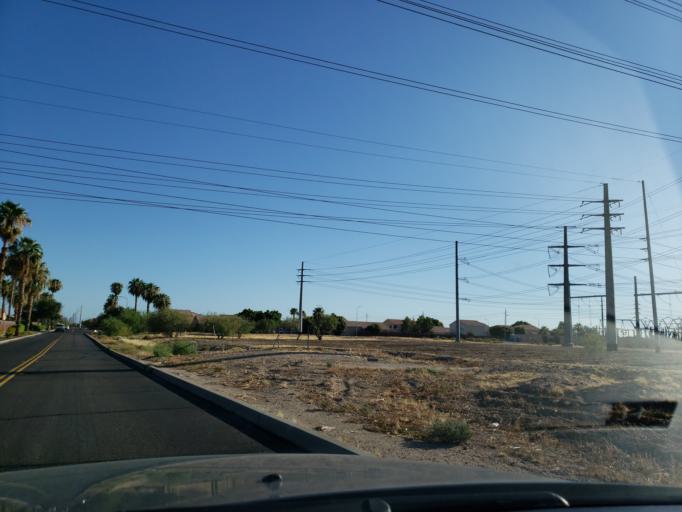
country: US
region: Arizona
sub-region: Maricopa County
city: Avondale
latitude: 33.4665
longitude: -112.3153
